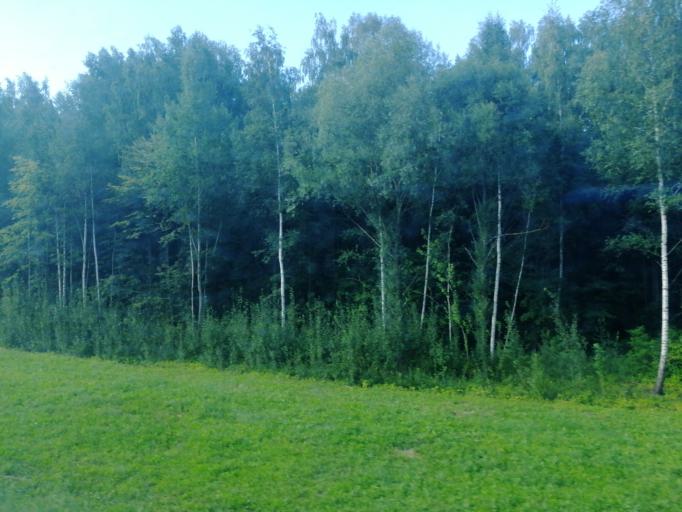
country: RU
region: Tula
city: Leninskiy
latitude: 54.2353
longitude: 37.3535
